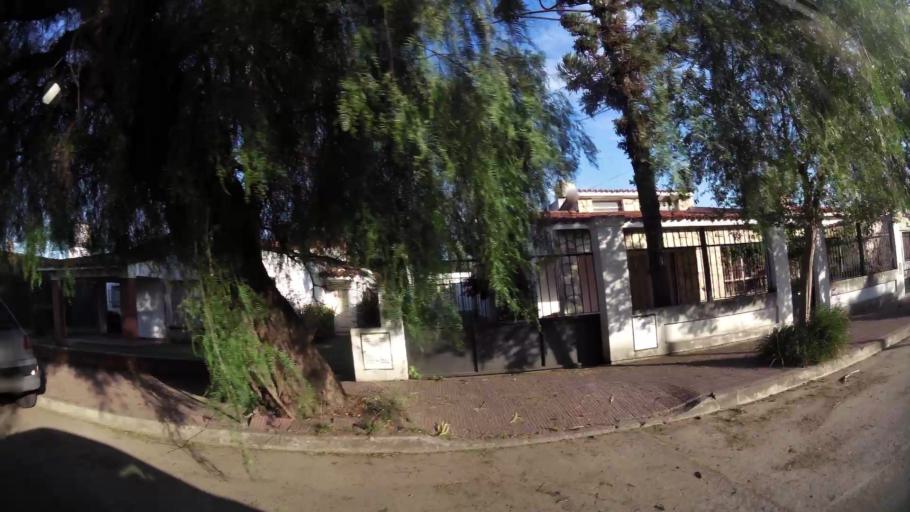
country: AR
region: Cordoba
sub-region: Departamento de Capital
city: Cordoba
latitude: -31.3859
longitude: -64.2250
